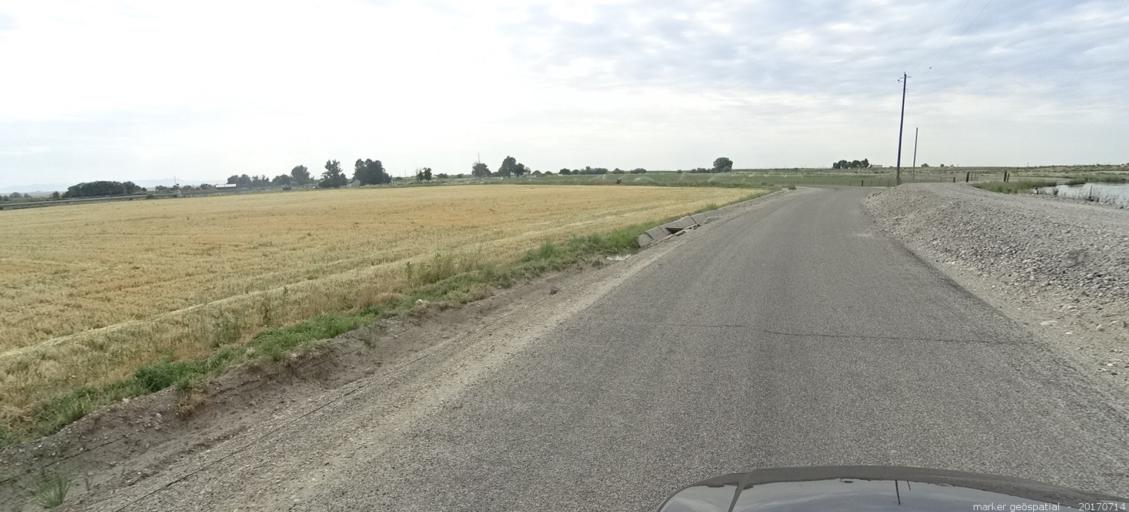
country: US
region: Idaho
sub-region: Ada County
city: Kuna
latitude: 43.4600
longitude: -116.3641
